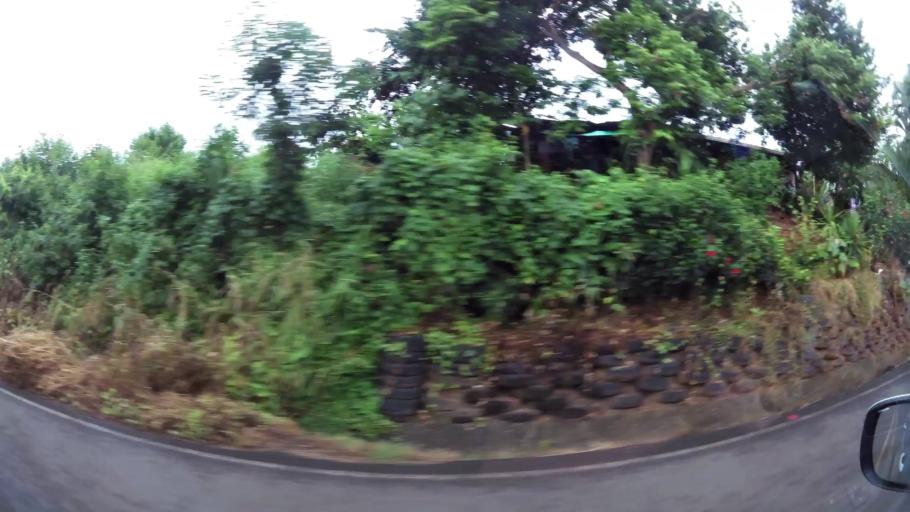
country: CR
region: Puntarenas
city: Esparza
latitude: 9.9792
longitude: -84.6220
